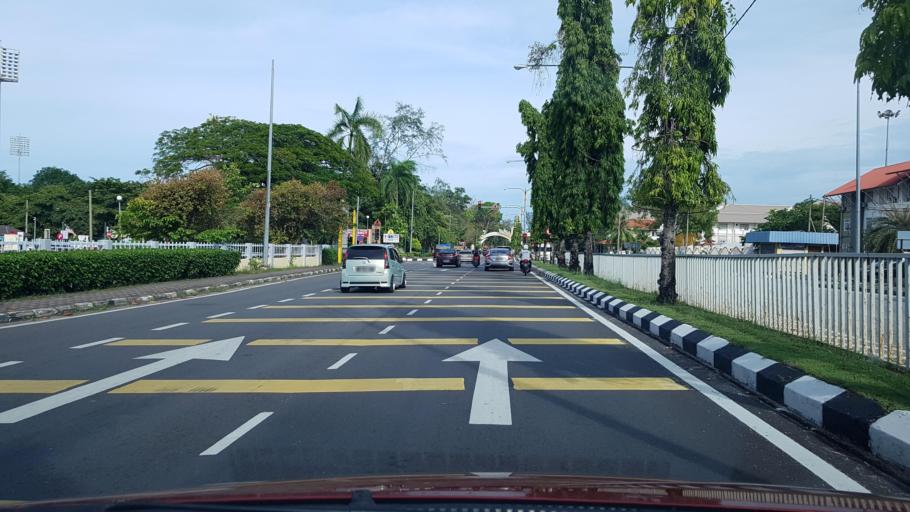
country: MY
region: Terengganu
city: Kuala Terengganu
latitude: 5.3243
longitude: 103.1500
